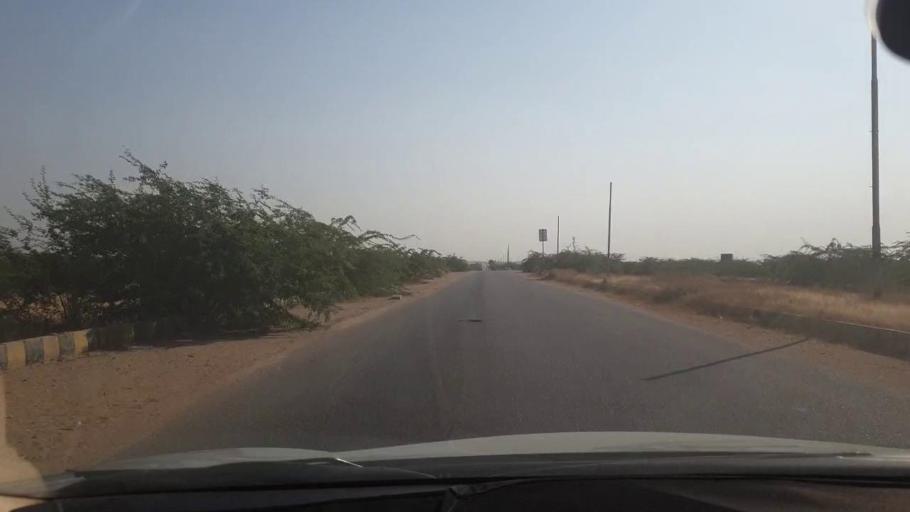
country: PK
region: Sindh
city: Malir Cantonment
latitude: 25.0630
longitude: 67.1391
